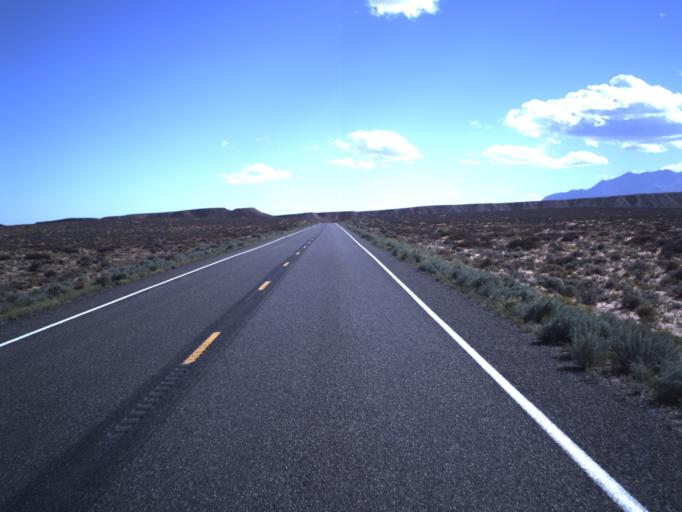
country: US
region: Utah
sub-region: Wayne County
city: Loa
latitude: 38.1693
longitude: -110.6238
